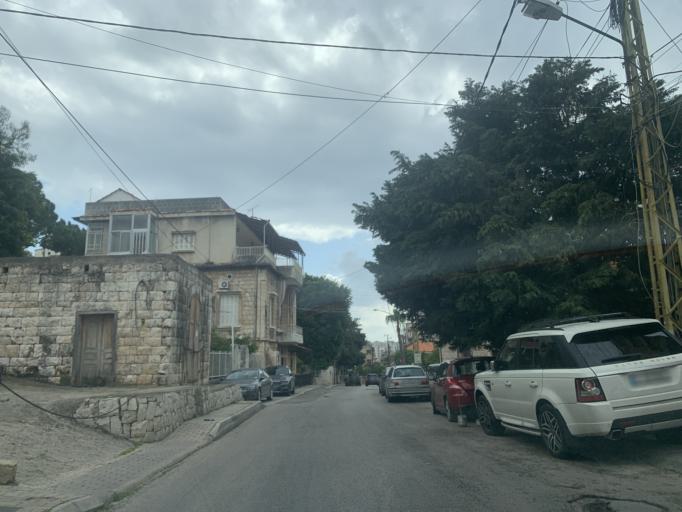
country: LB
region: Mont-Liban
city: Djounie
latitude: 33.9831
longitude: 35.6391
